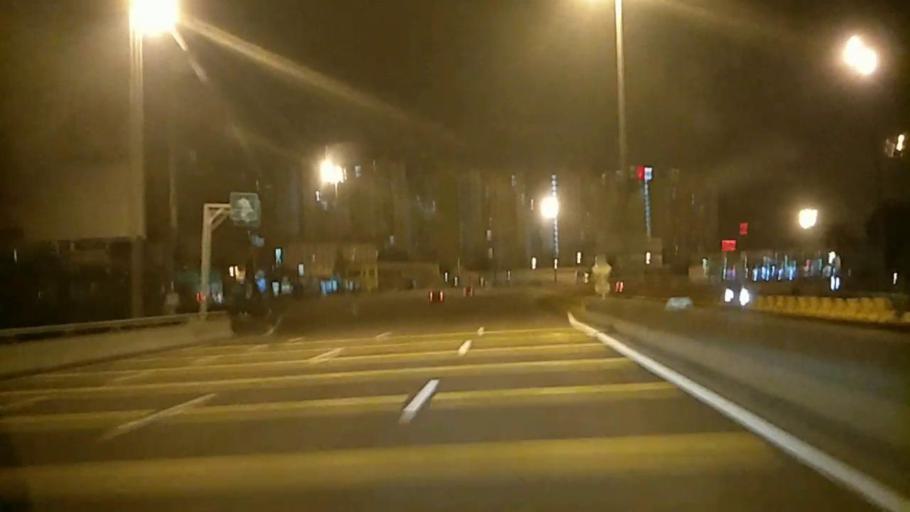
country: MY
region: Selangor
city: Subang Jaya
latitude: 3.0582
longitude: 101.6150
